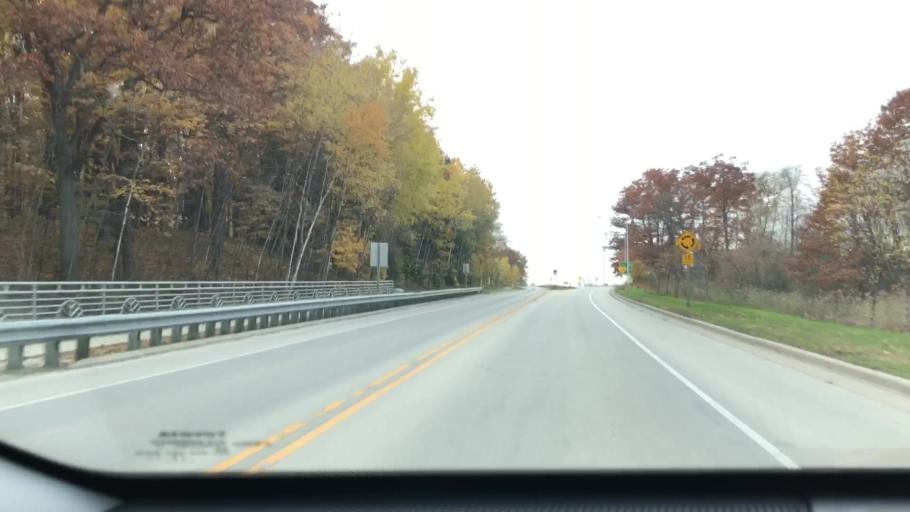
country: US
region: Wisconsin
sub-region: Brown County
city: Oneida
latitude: 44.5004
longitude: -88.1901
